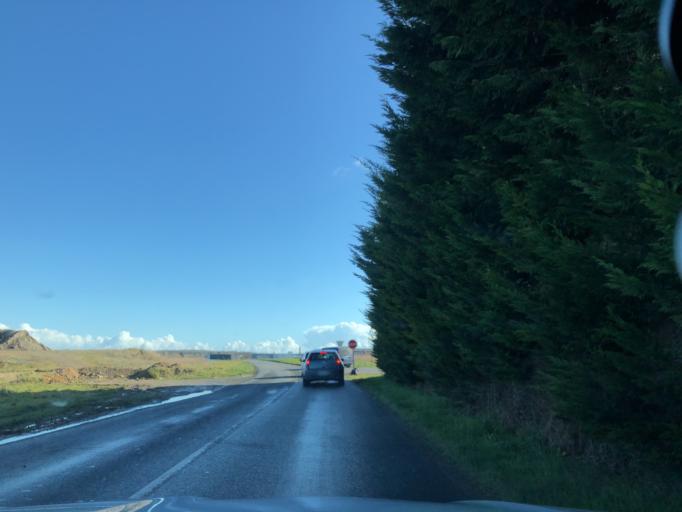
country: FR
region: Lower Normandy
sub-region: Departement du Calvados
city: Epron
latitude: 49.2217
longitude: -0.3633
